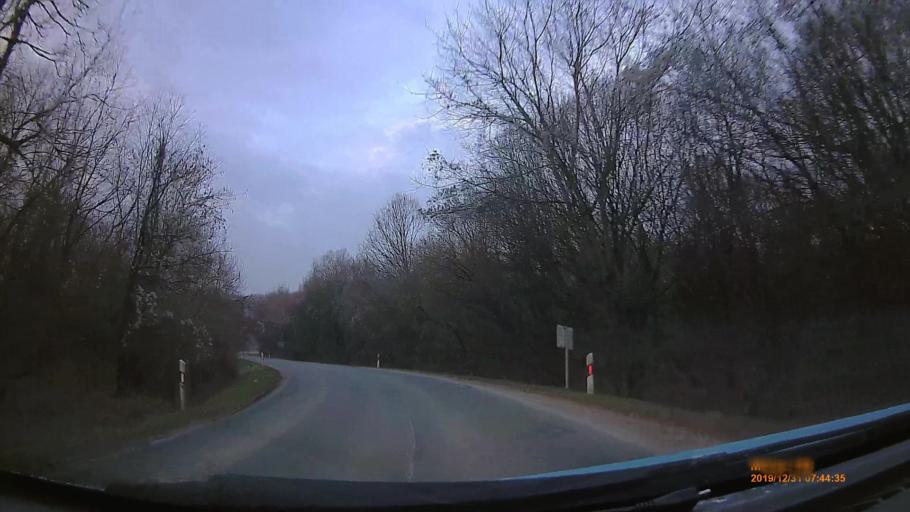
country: HU
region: Heves
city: Recsk
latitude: 47.9269
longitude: 20.1427
